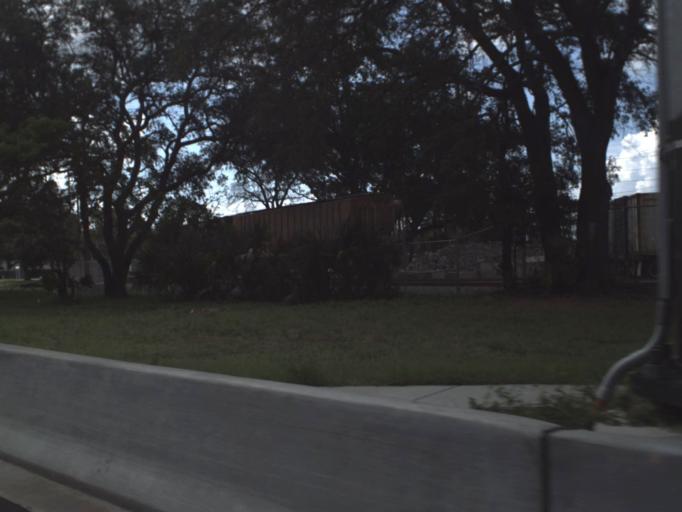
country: US
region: Florida
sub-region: Bay County
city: Upper Grand Lagoon
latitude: 30.1824
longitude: -85.7263
